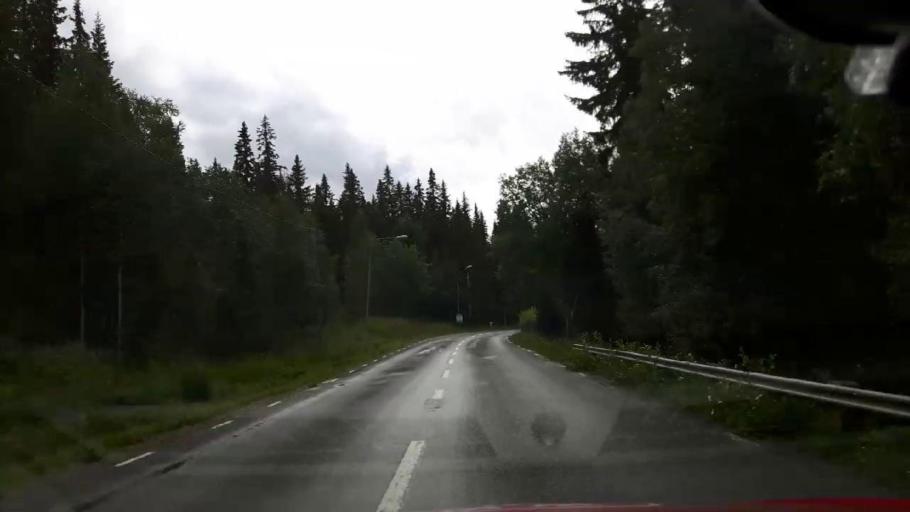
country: NO
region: Nord-Trondelag
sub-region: Lierne
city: Sandvika
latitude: 64.4992
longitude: 14.1512
